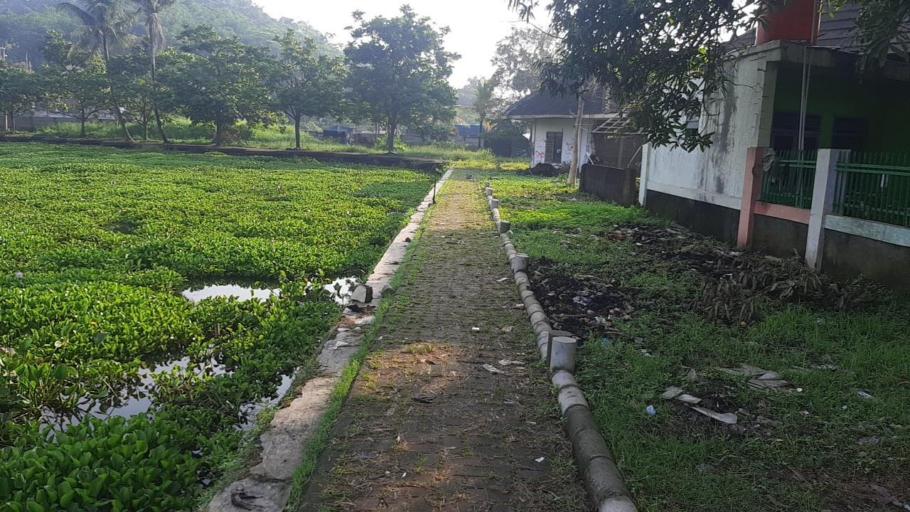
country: ID
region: West Java
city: Citeureup
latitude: -6.4638
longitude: 106.8911
